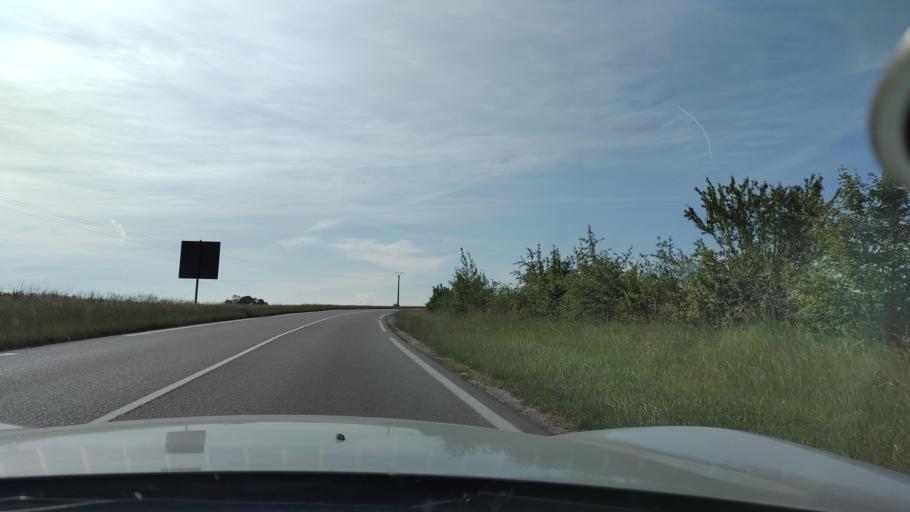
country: FR
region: Ile-de-France
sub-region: Departement de Seine-et-Marne
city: Jouy-le-Chatel
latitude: 48.6683
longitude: 3.1342
